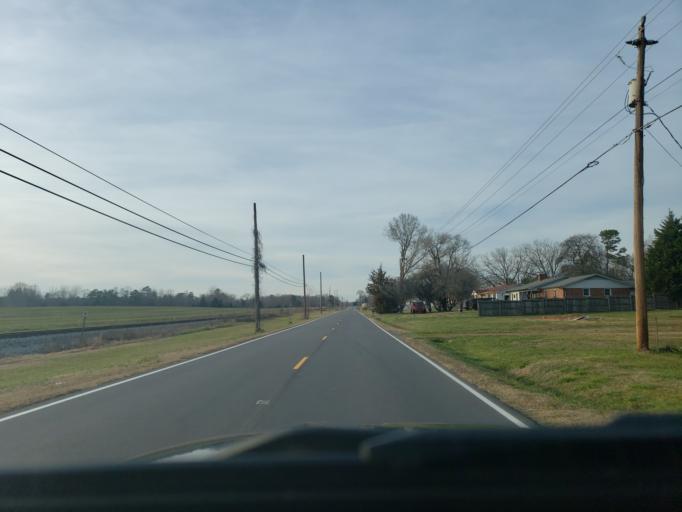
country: US
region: North Carolina
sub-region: Cleveland County
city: Boiling Springs
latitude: 35.3124
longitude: -81.7376
